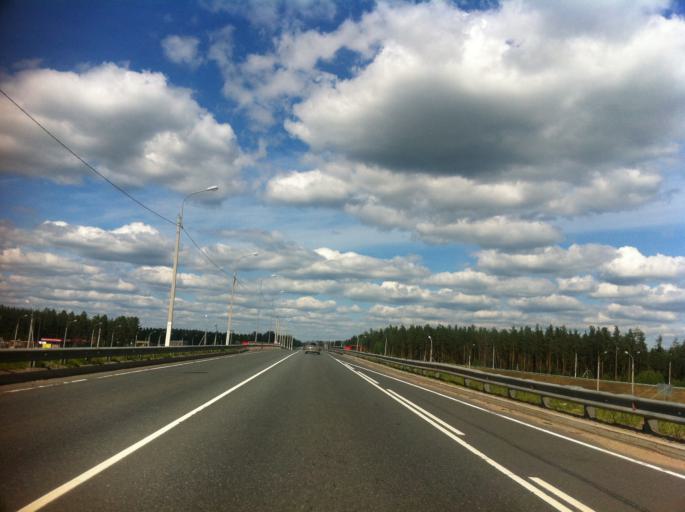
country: RU
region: Leningrad
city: Luga
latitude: 58.7297
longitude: 29.8821
